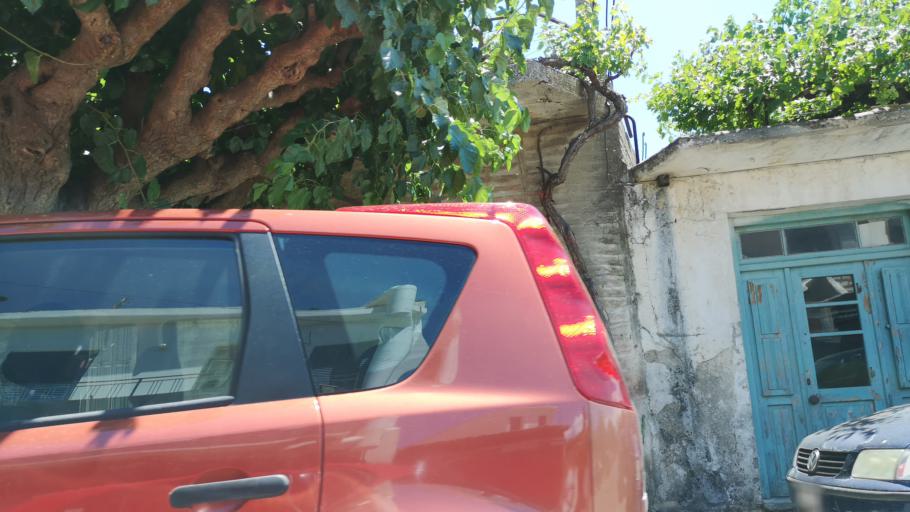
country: GR
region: Crete
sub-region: Nomos Lasithiou
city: Neapoli
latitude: 35.2594
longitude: 25.6495
